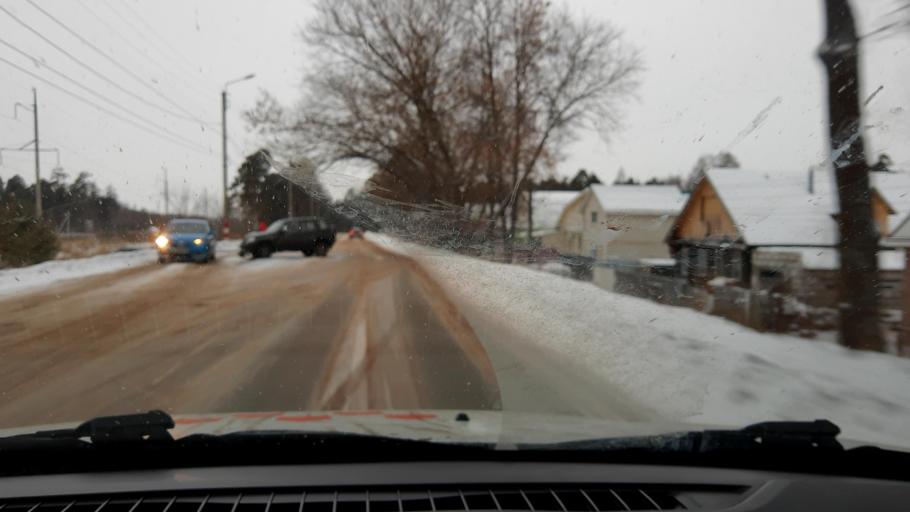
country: RU
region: Nizjnij Novgorod
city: Bor
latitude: 56.3278
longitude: 44.1287
